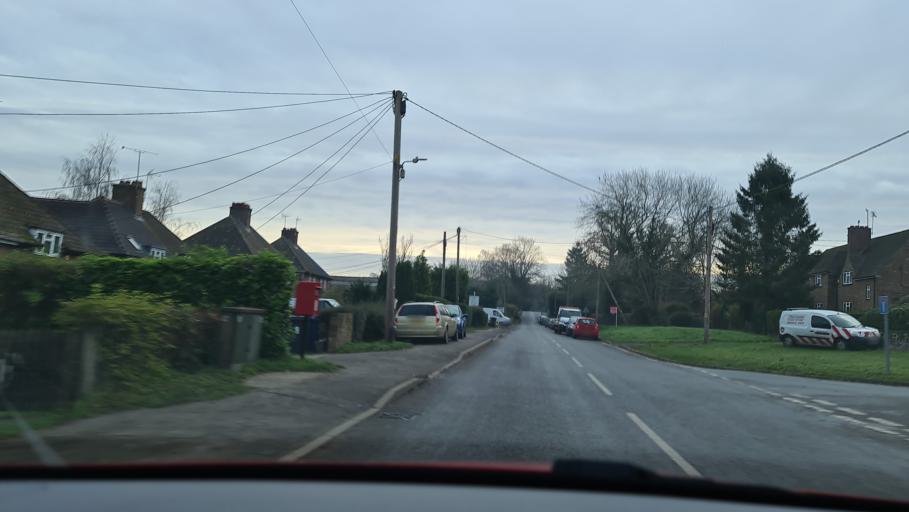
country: GB
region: England
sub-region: Buckinghamshire
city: Great Missenden
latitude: 51.7077
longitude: -0.7149
